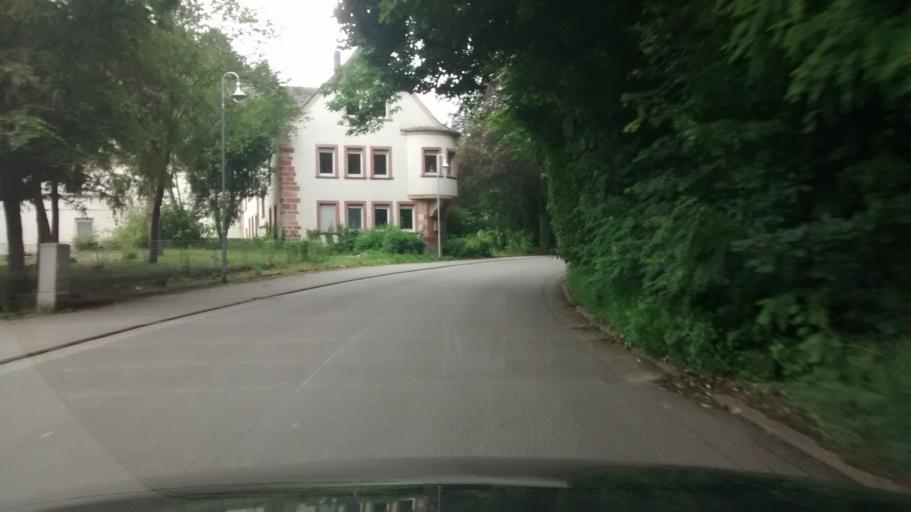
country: DE
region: Rheinland-Pfalz
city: Bad Bergzabern
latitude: 49.1000
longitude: 7.9827
